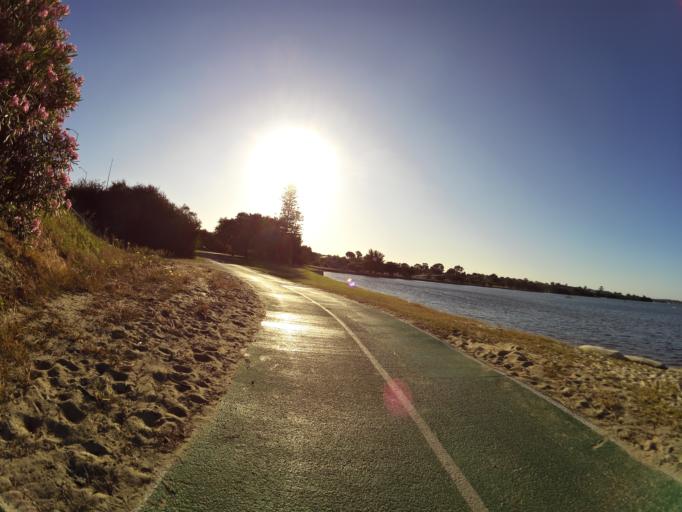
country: AU
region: Western Australia
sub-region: South Perth
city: Manning
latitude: -32.0109
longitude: 115.8541
